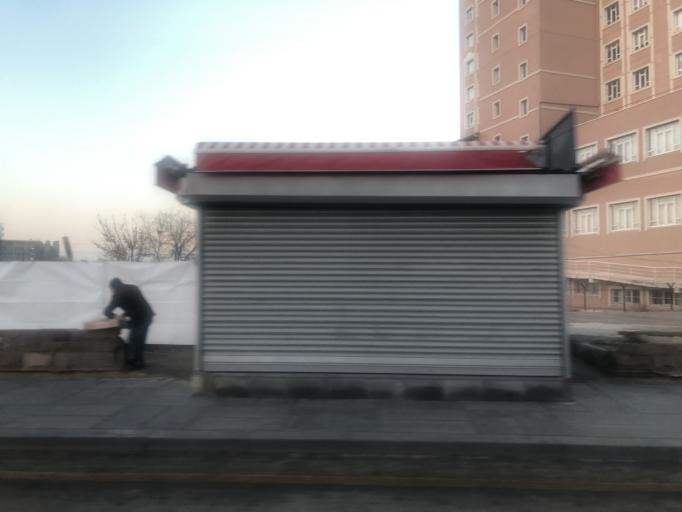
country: TR
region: Ankara
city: Ankara
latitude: 39.9516
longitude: 32.8576
